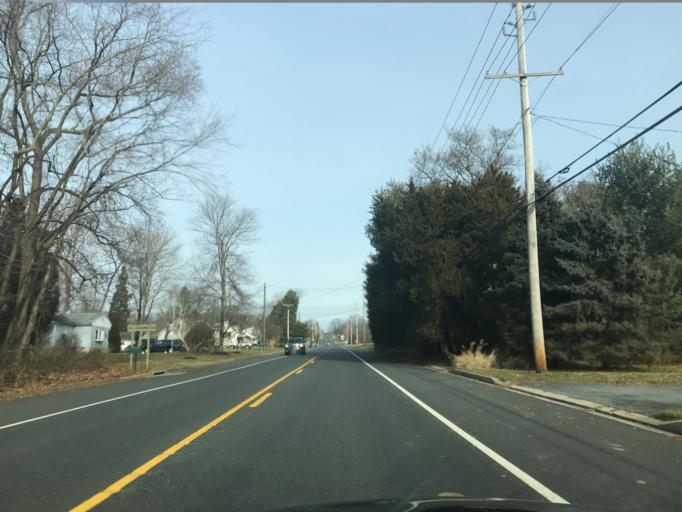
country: US
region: Maryland
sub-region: Harford County
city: Aberdeen
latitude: 39.5516
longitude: -76.1672
